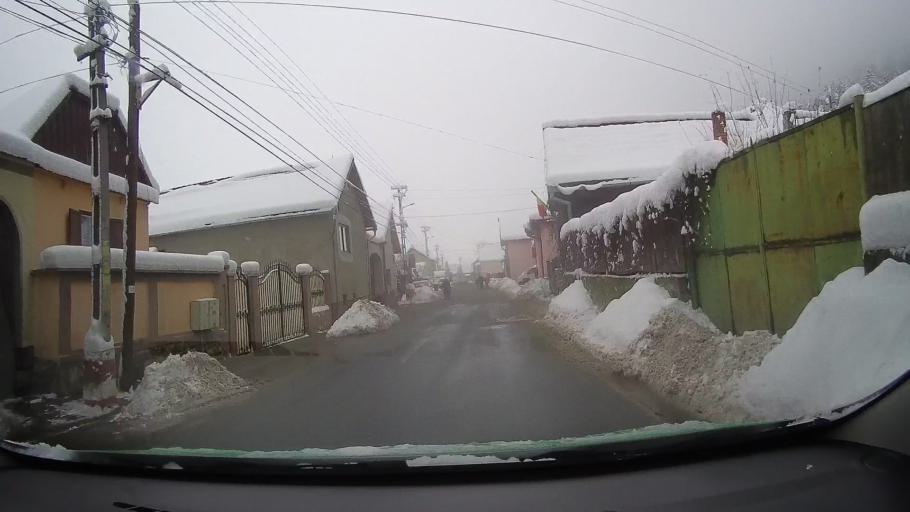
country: RO
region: Sibiu
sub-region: Oras Saliste
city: Saliste
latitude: 45.7960
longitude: 23.8701
